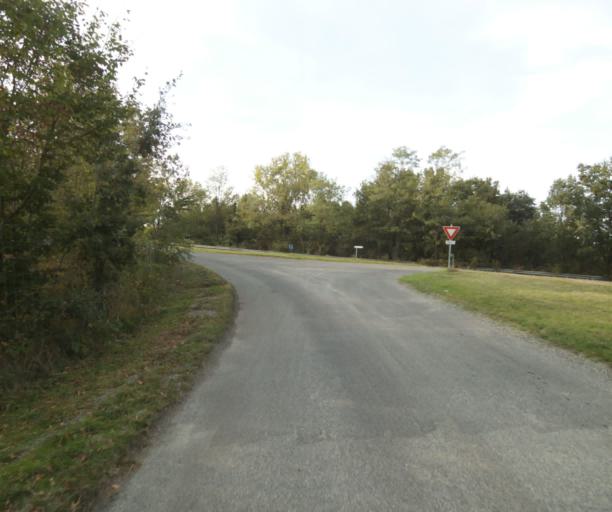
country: FR
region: Midi-Pyrenees
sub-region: Departement du Tarn-et-Garonne
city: Campsas
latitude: 43.8907
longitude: 1.3193
